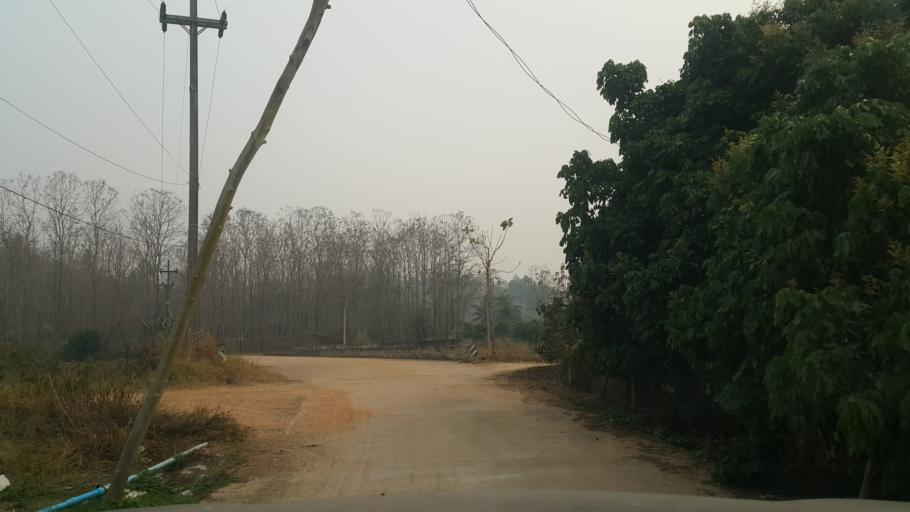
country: TH
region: Lamphun
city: Mae Tha
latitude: 18.5090
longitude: 99.2130
